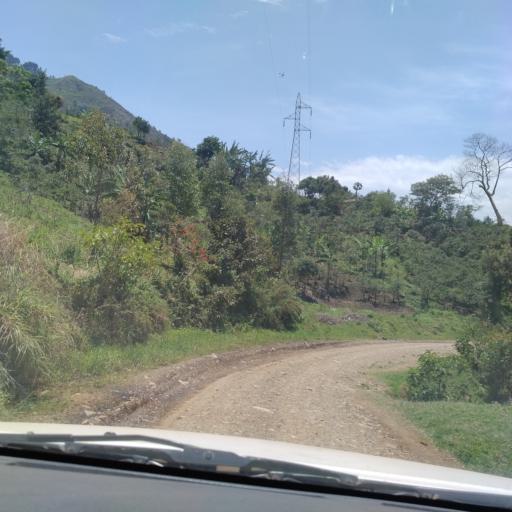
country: CD
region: Nord Kivu
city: Sake
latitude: -1.9143
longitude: 28.9509
